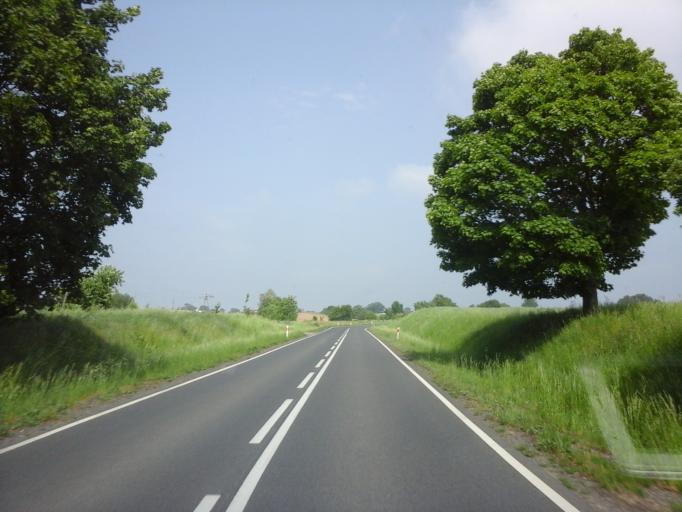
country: PL
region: West Pomeranian Voivodeship
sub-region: Powiat choszczenski
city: Choszczno
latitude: 53.1229
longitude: 15.3635
